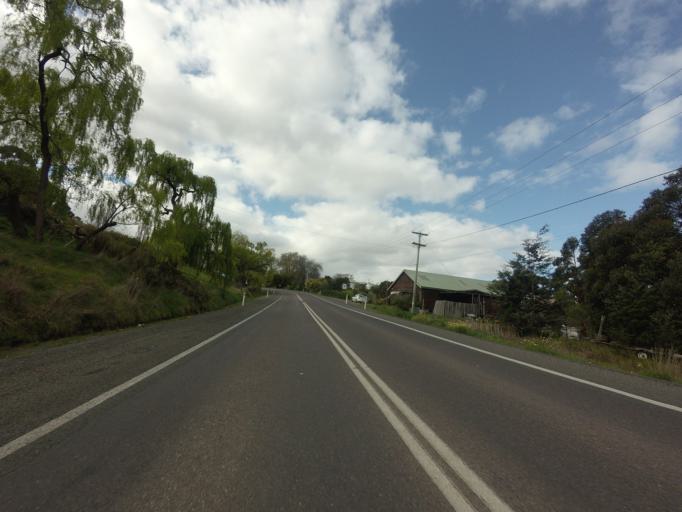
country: AU
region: Tasmania
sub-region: Huon Valley
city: Franklin
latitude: -43.1297
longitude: 146.9893
